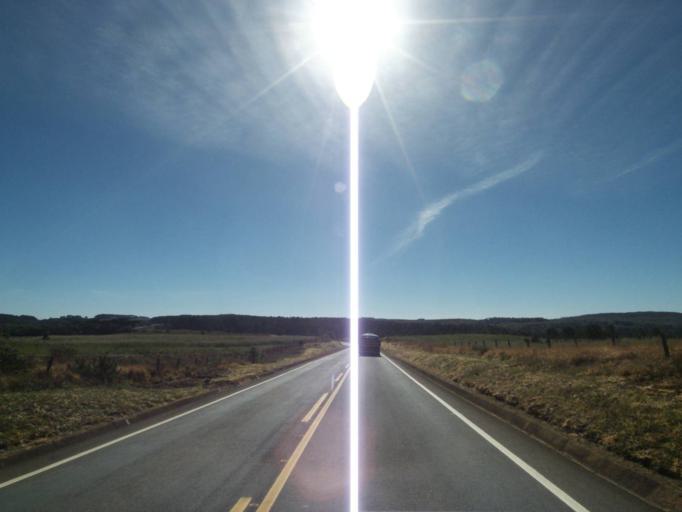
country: BR
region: Parana
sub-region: Castro
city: Castro
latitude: -24.7347
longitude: -50.1817
